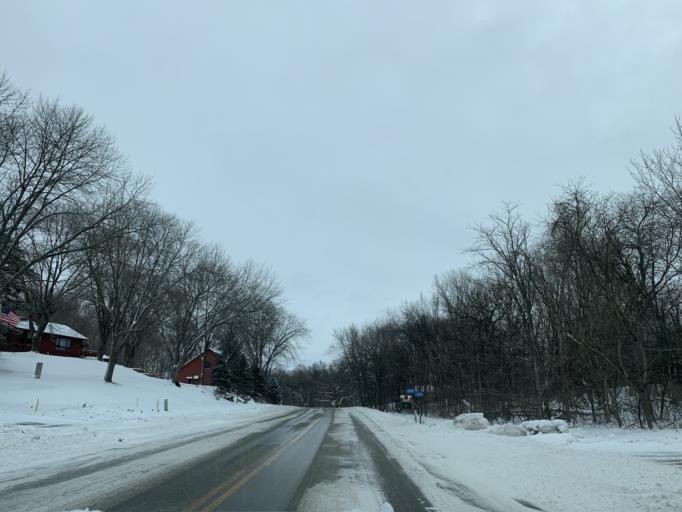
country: US
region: Minnesota
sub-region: Carver County
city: Chaska
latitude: 44.7866
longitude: -93.6166
